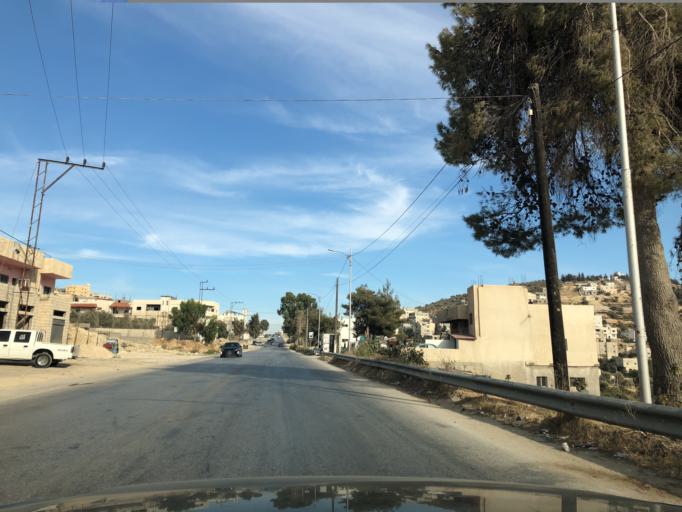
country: JO
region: Irbid
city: Sakib
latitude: 32.2794
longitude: 35.7986
